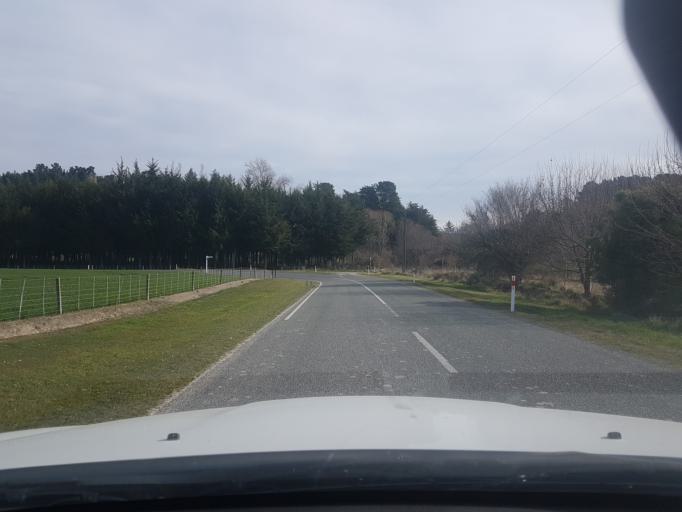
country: NZ
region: Canterbury
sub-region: Timaru District
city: Pleasant Point
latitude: -44.1293
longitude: 171.1826
